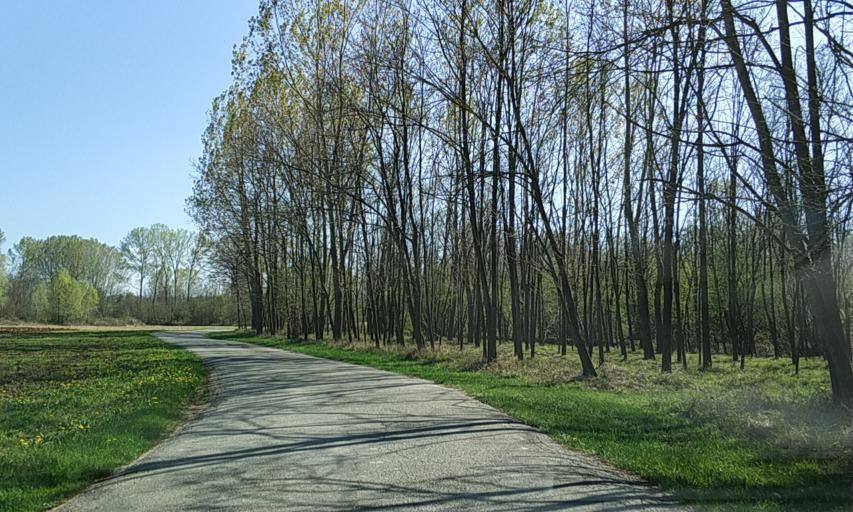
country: IT
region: Piedmont
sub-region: Provincia di Torino
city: Rivara
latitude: 45.3129
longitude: 7.6411
